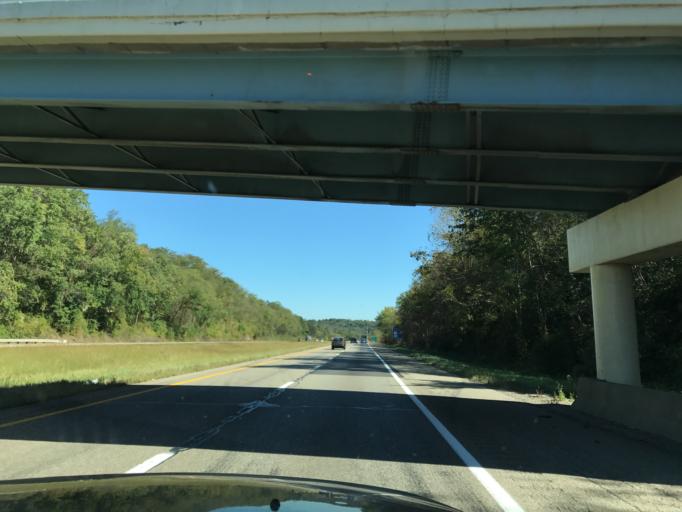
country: US
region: Ohio
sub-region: Muskingum County
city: Zanesville
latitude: 39.9468
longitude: -82.0677
